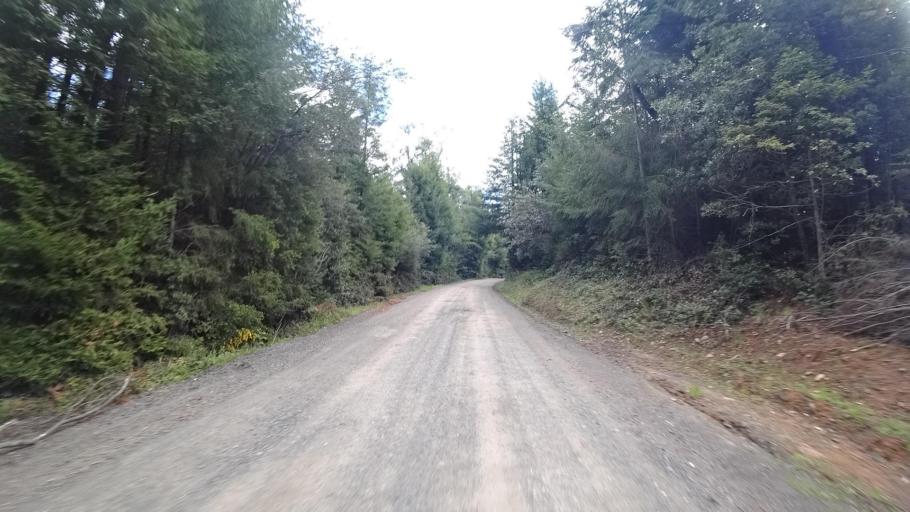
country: US
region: California
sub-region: Humboldt County
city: Blue Lake
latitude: 40.7708
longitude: -123.9568
